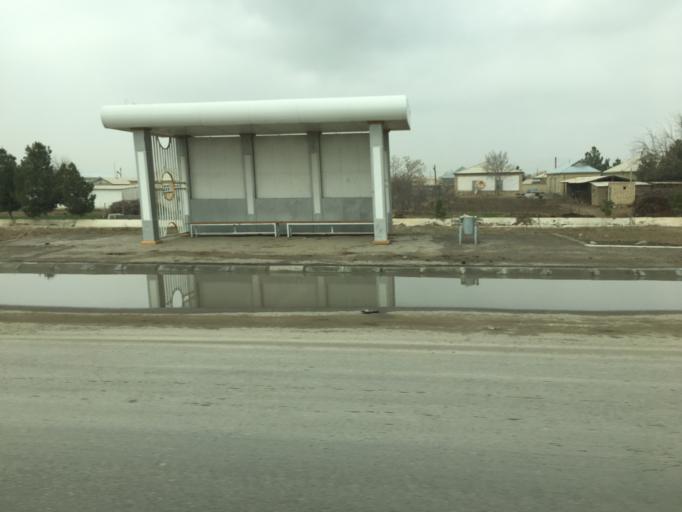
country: TM
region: Mary
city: Mary
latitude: 37.5615
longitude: 61.7583
